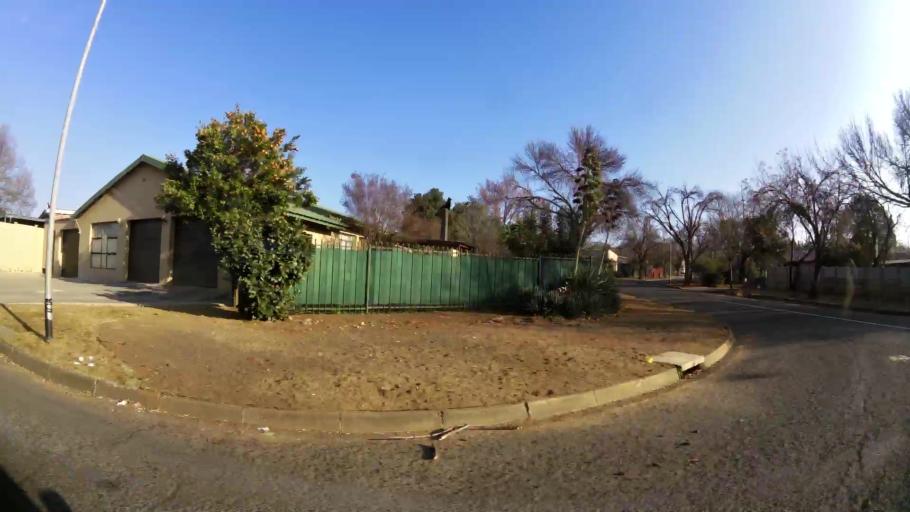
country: ZA
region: Orange Free State
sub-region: Mangaung Metropolitan Municipality
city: Bloemfontein
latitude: -29.1508
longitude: 26.2005
